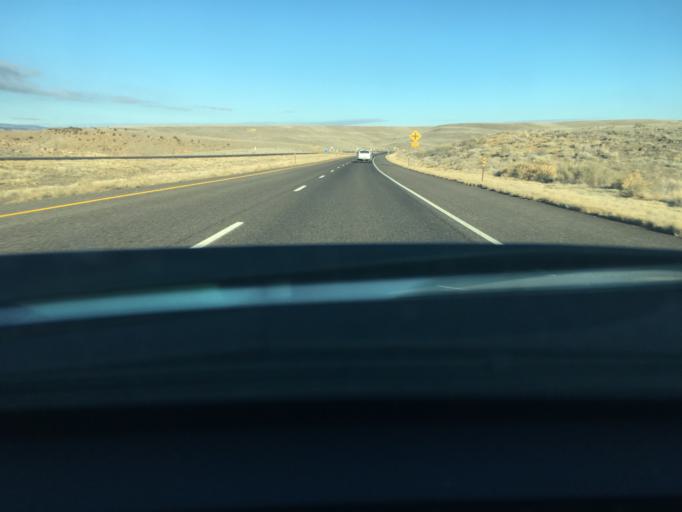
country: US
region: Colorado
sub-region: Delta County
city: Delta
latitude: 38.8060
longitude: -108.2758
